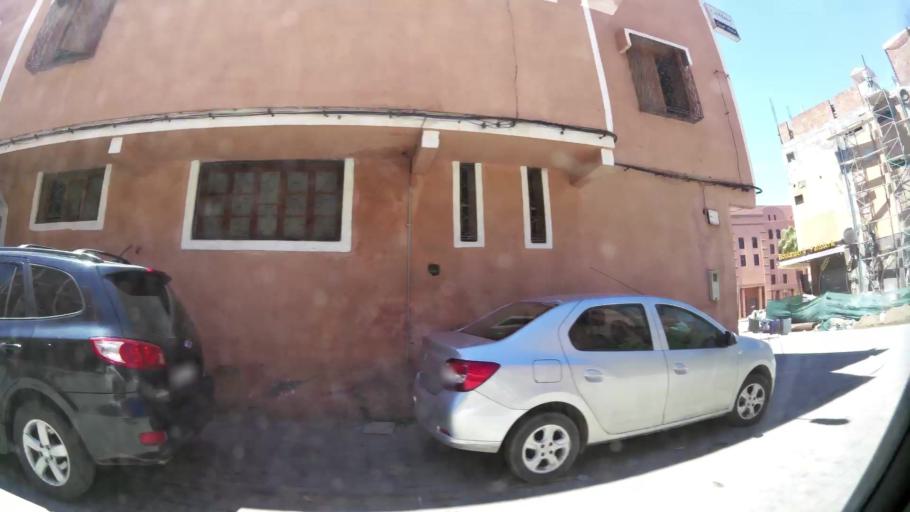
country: MA
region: Marrakech-Tensift-Al Haouz
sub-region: Marrakech
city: Marrakesh
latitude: 31.6497
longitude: -8.0004
